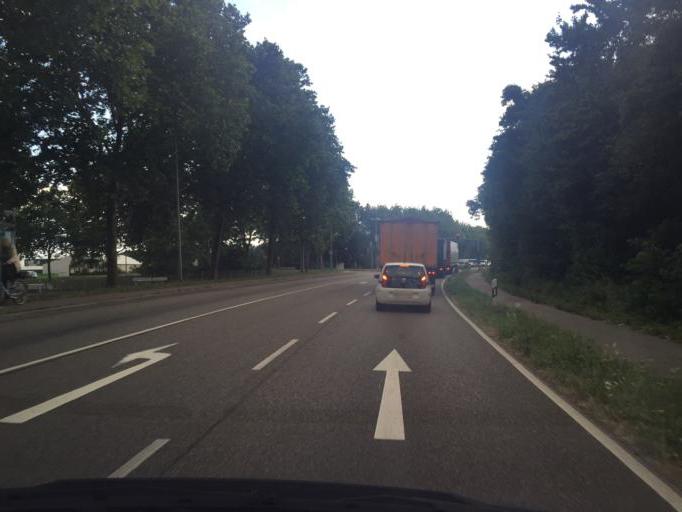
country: DE
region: Baden-Wuerttemberg
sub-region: Karlsruhe Region
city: Bruchsal
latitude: 49.1240
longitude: 8.5788
